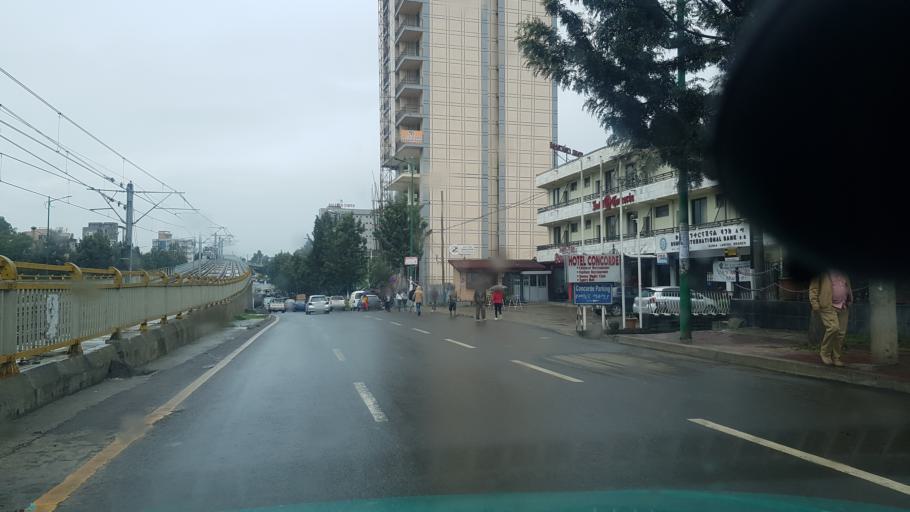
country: ET
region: Adis Abeba
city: Addis Ababa
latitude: 8.9901
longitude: 38.7592
